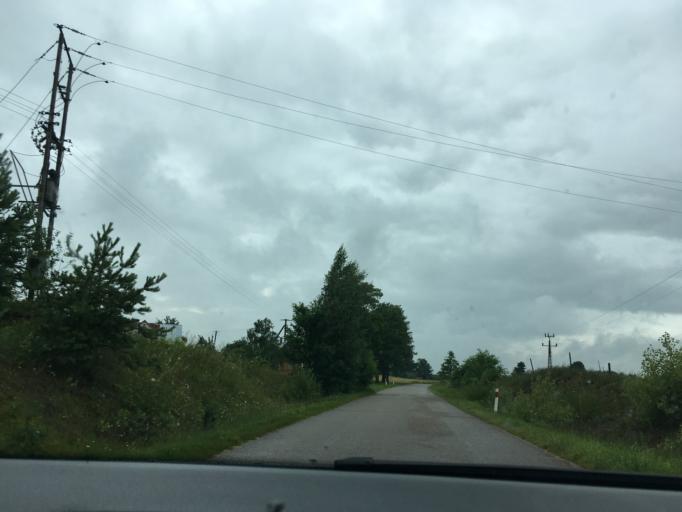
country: PL
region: Podlasie
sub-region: Powiat sejnenski
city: Krasnopol
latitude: 54.0963
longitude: 23.2291
